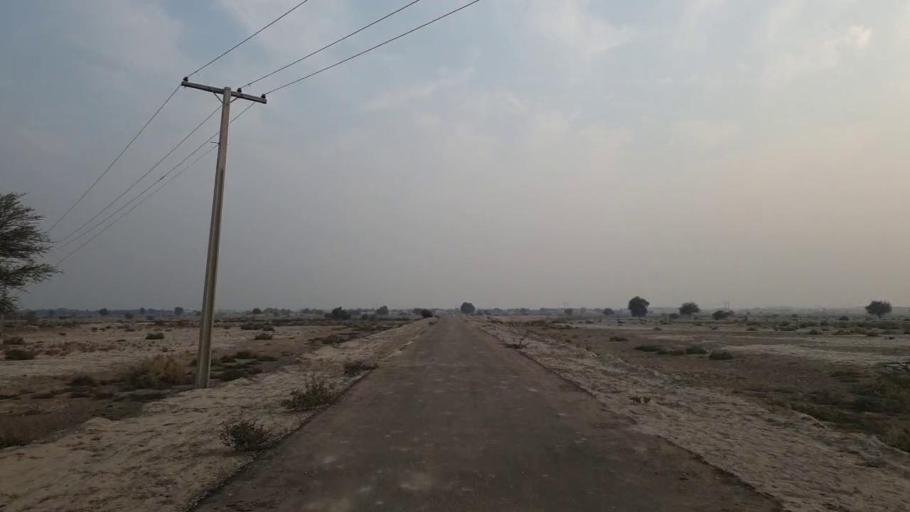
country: PK
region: Sindh
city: Sann
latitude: 26.1779
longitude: 67.9903
